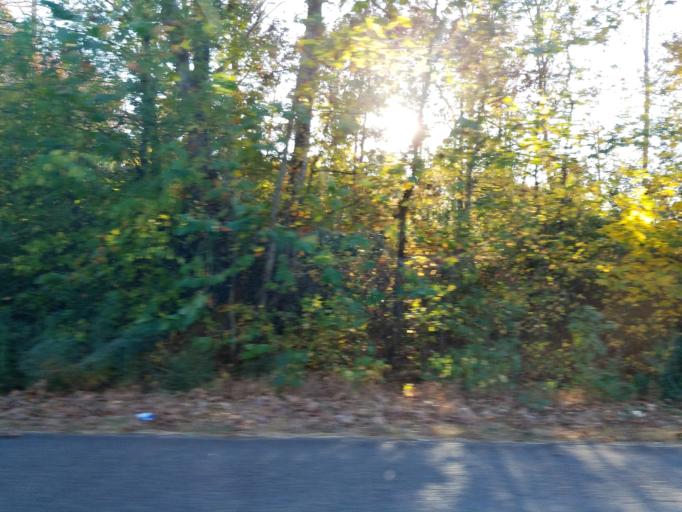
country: US
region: Georgia
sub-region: Bartow County
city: Euharlee
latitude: 34.2247
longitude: -84.9372
